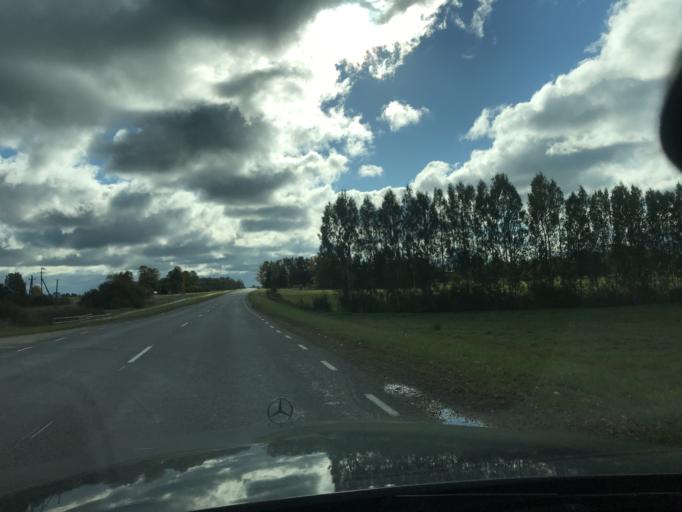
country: EE
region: Vorumaa
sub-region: Antsla vald
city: Vana-Antsla
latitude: 57.9398
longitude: 26.3087
